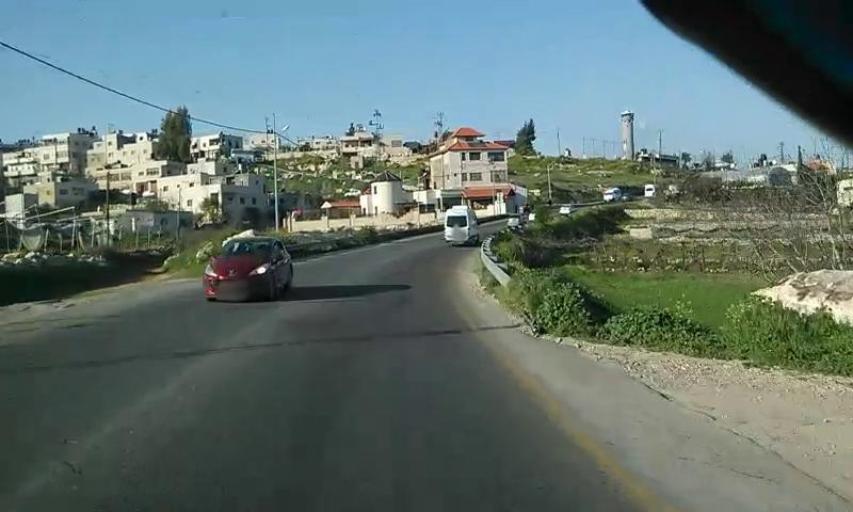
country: PS
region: West Bank
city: Bayt Ummar
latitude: 31.6173
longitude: 35.1150
